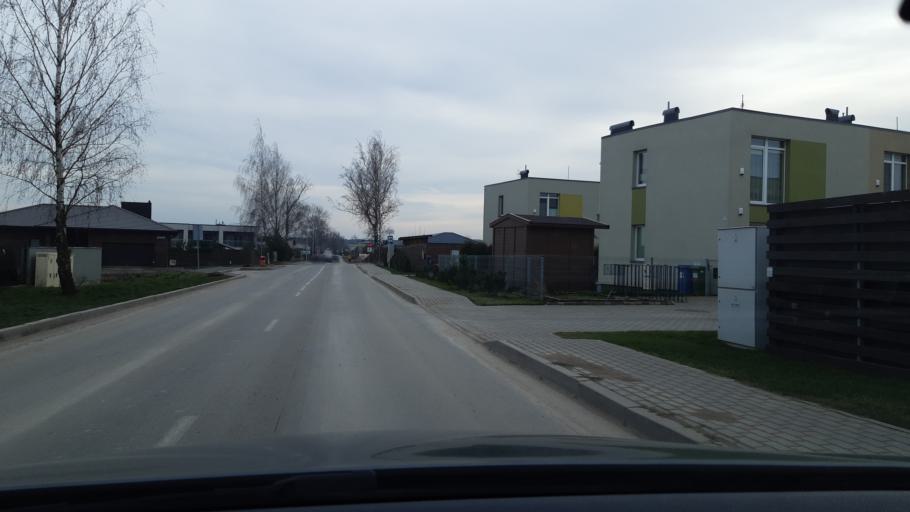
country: LT
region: Kauno apskritis
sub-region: Kauno rajonas
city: Akademija (Kaunas)
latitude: 54.9487
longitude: 23.8285
